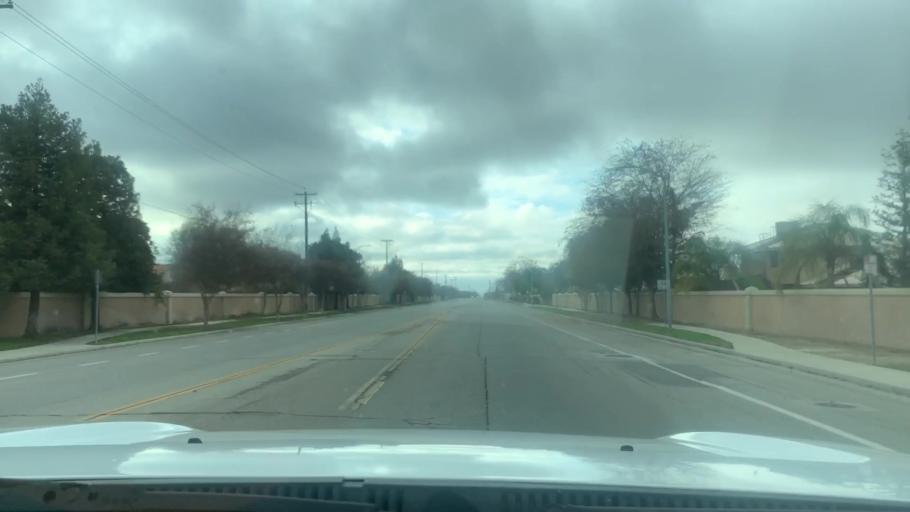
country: US
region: California
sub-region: Kern County
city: Shafter
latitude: 35.4999
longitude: -119.2893
